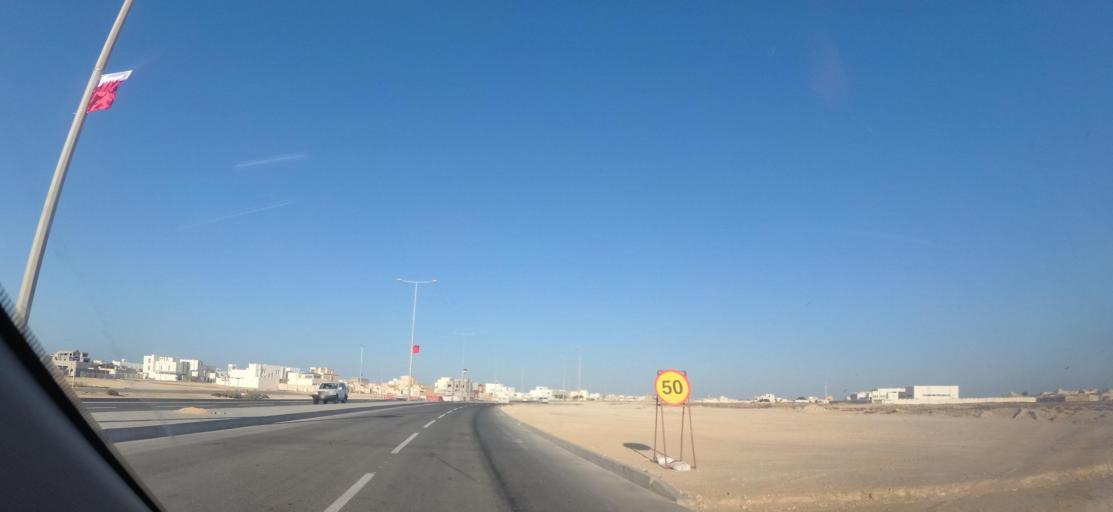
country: QA
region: Madinat ash Shamal
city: Madinat ash Shamal
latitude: 26.1202
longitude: 51.1867
